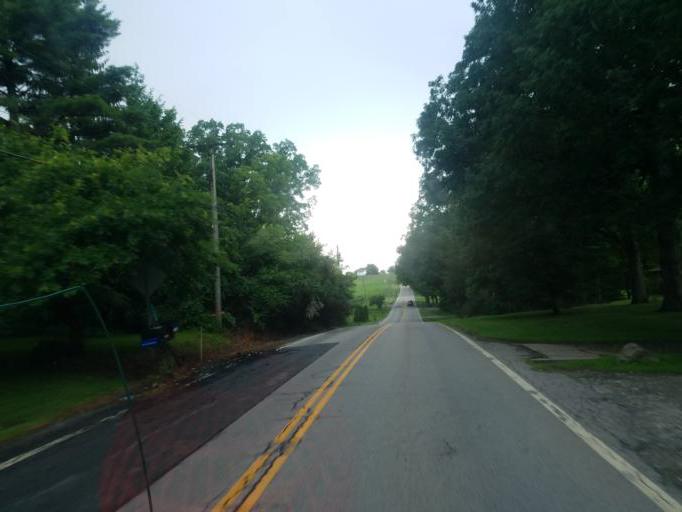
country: US
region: Ohio
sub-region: Wayne County
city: Rittman
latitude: 40.9463
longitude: -81.7678
